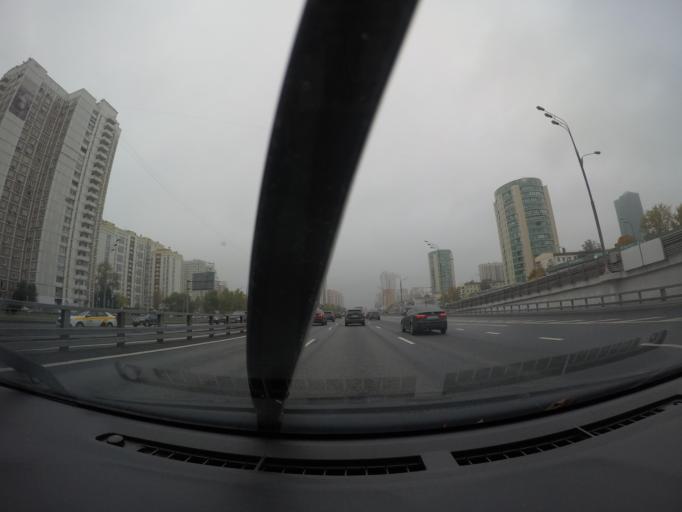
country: RU
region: Moskovskaya
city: Khoroshevo-Mnevniki
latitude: 55.7766
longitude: 37.4677
